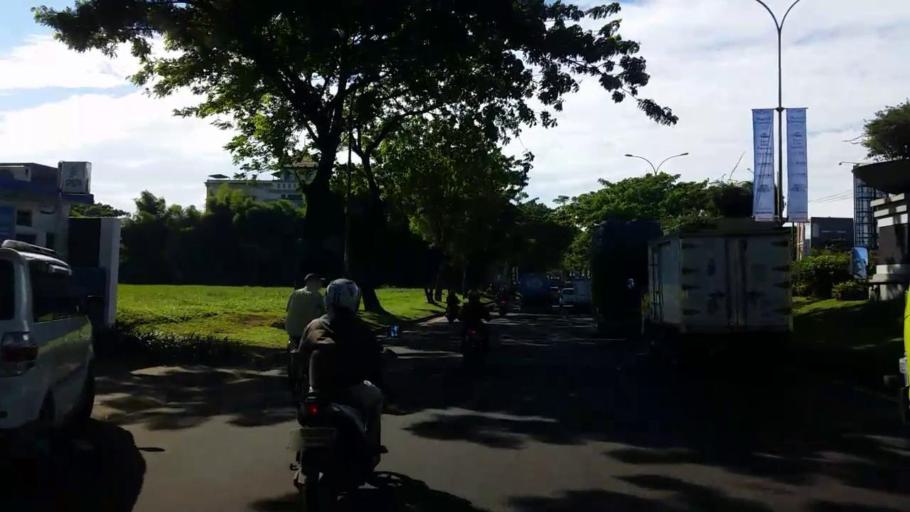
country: ID
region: West Java
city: Serpong
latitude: -6.3001
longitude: 106.6681
